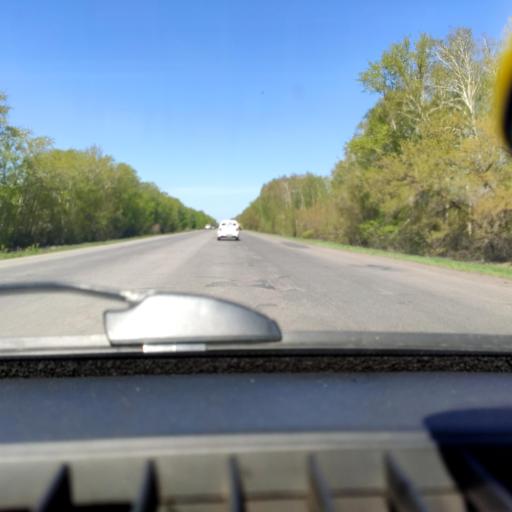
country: RU
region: Samara
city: Tol'yatti
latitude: 53.6346
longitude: 49.4184
